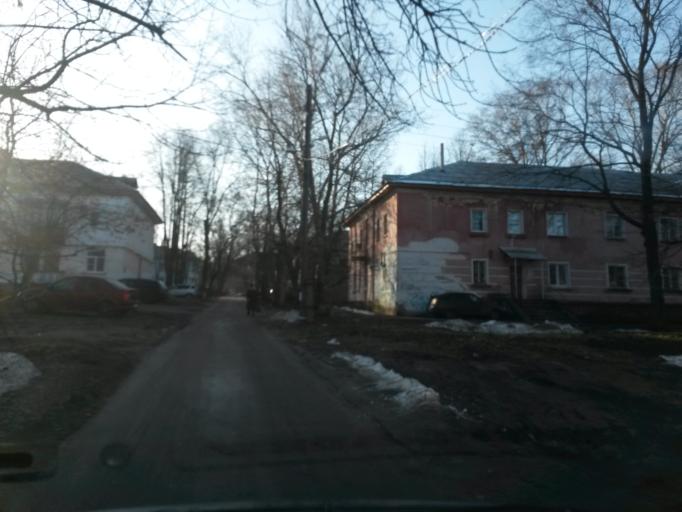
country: RU
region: Jaroslavl
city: Yaroslavl
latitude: 57.5820
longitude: 39.8409
